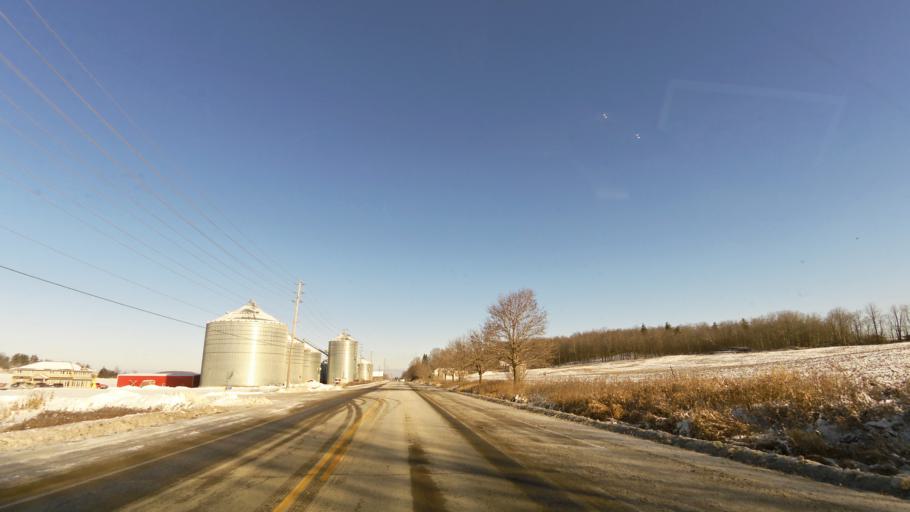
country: CA
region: Ontario
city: Quinte West
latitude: 44.2193
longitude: -77.8273
